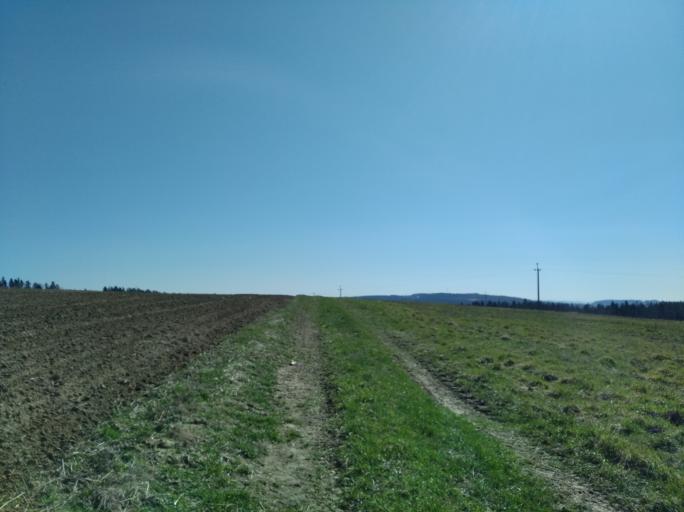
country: PL
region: Subcarpathian Voivodeship
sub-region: Powiat strzyzowski
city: Jawornik
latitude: 49.8392
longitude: 21.8528
